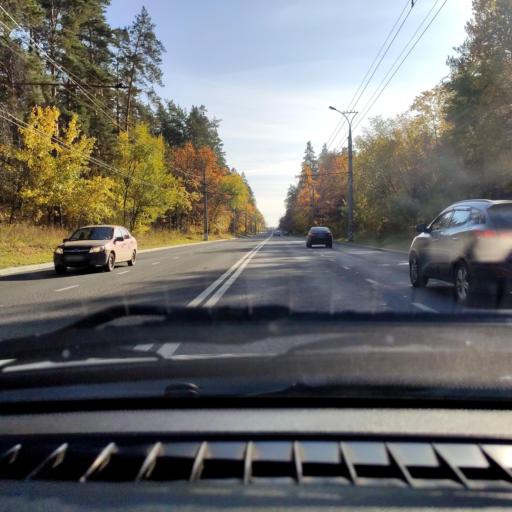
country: RU
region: Samara
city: Zhigulevsk
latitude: 53.4995
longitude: 49.4633
